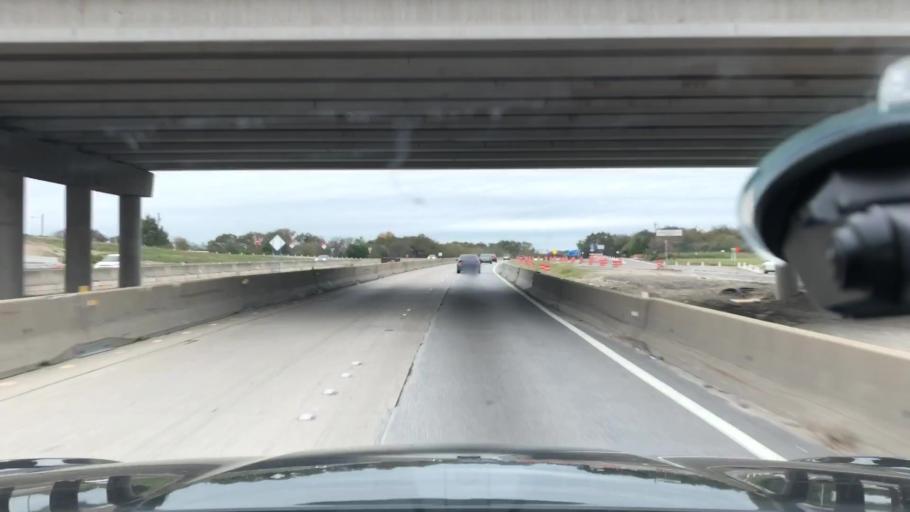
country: US
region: Texas
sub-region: Ellis County
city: Waxahachie
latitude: 32.3997
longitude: -96.8724
